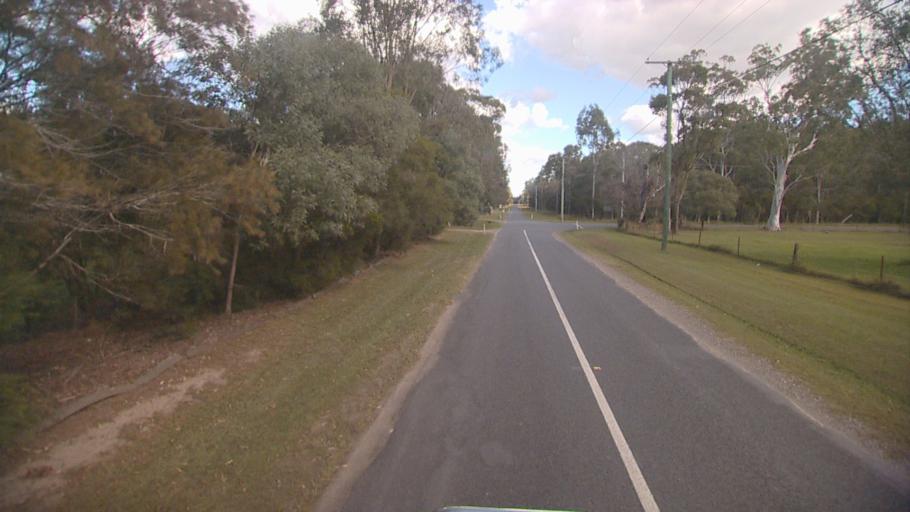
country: AU
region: Queensland
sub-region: Gold Coast
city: Yatala
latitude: -27.6607
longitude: 153.2414
